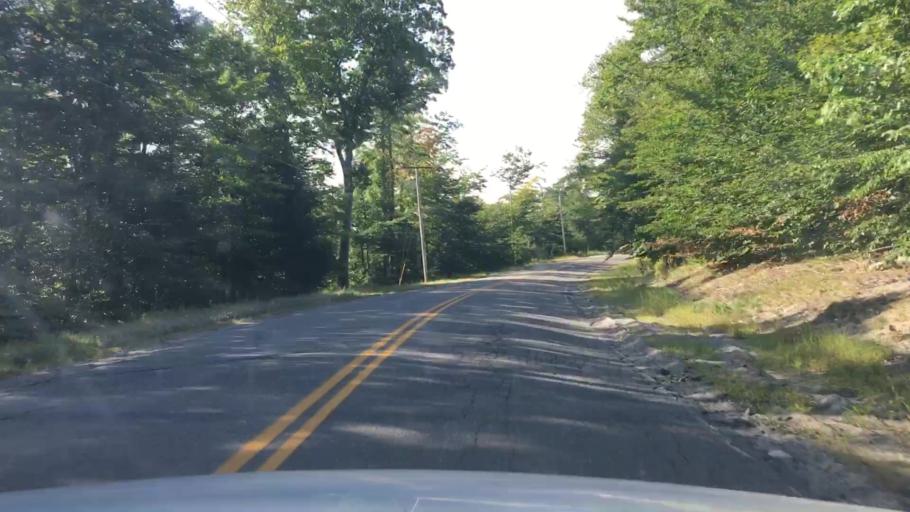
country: US
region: Maine
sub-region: Penobscot County
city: Enfield
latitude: 45.2256
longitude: -68.5405
